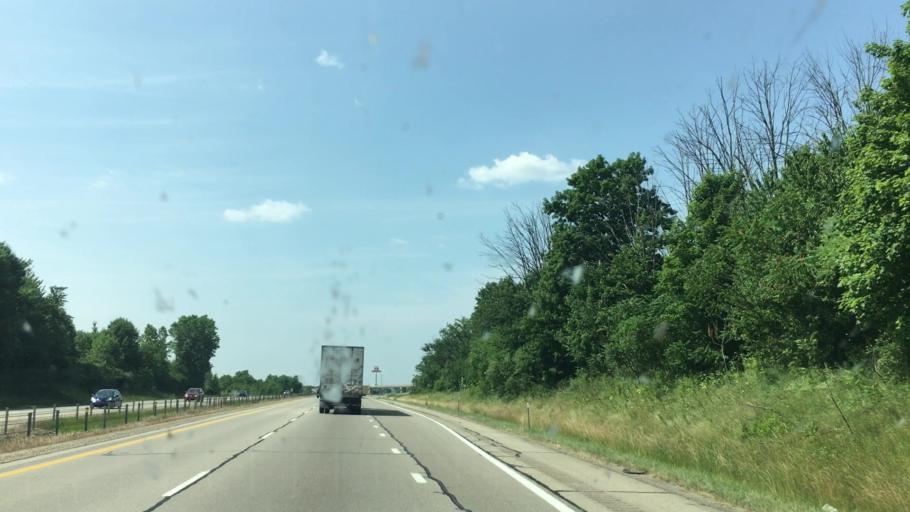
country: US
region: Michigan
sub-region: Allegan County
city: Wayland
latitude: 42.7194
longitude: -85.6686
